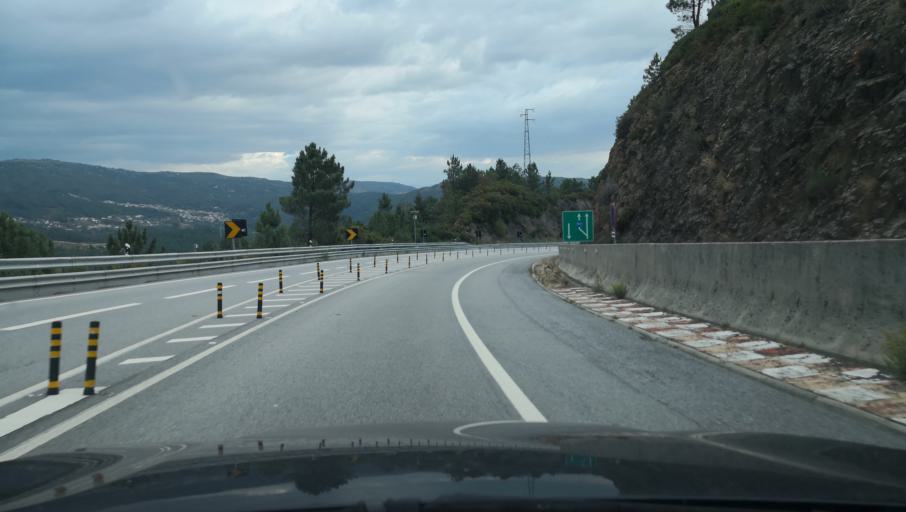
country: PT
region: Porto
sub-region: Baiao
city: Valadares
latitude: 41.2623
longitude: -7.9473
